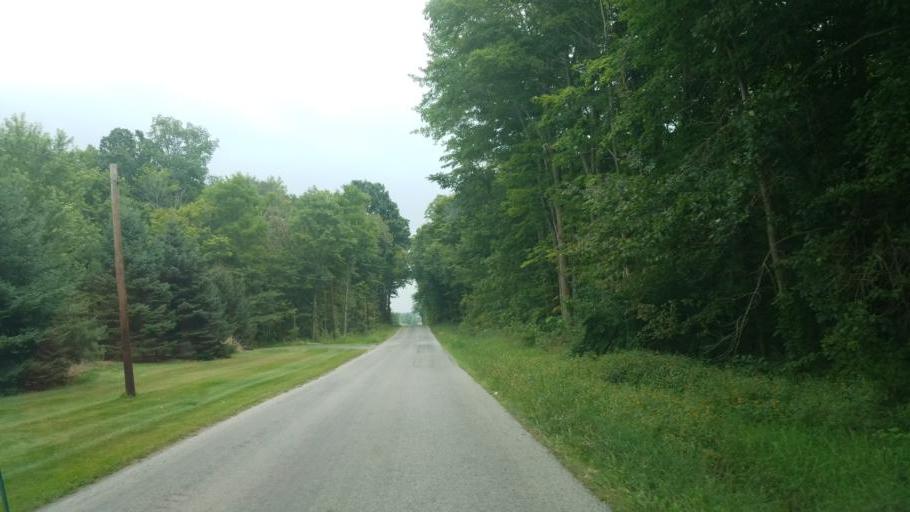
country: US
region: Ohio
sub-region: Medina County
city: Westfield Center
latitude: 40.9592
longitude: -81.9691
